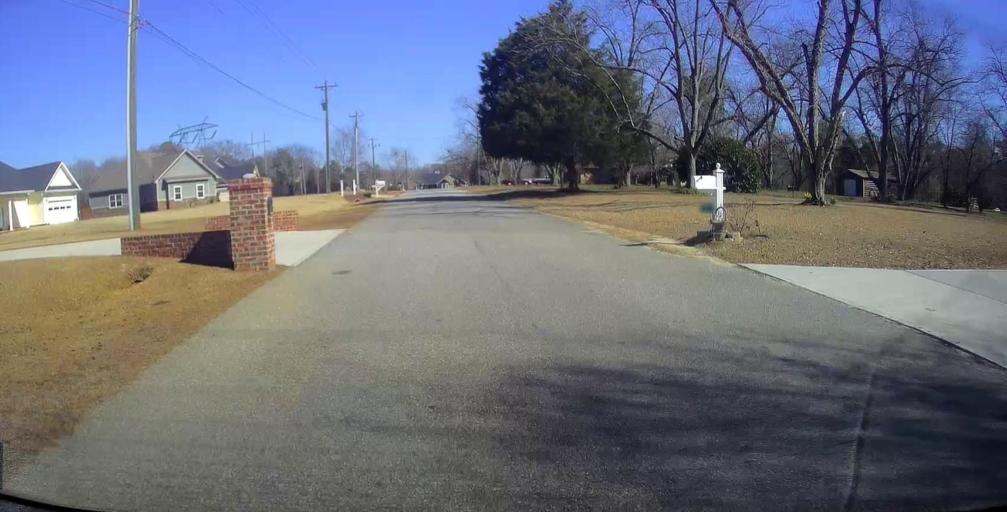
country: US
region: Georgia
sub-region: Peach County
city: Byron
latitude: 32.6356
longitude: -83.7592
